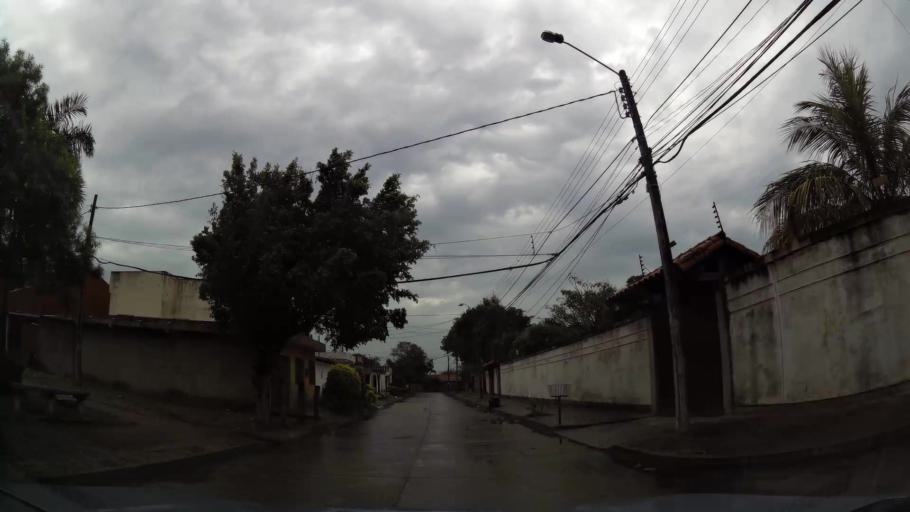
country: BO
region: Santa Cruz
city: Santa Cruz de la Sierra
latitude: -17.7987
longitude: -63.1575
